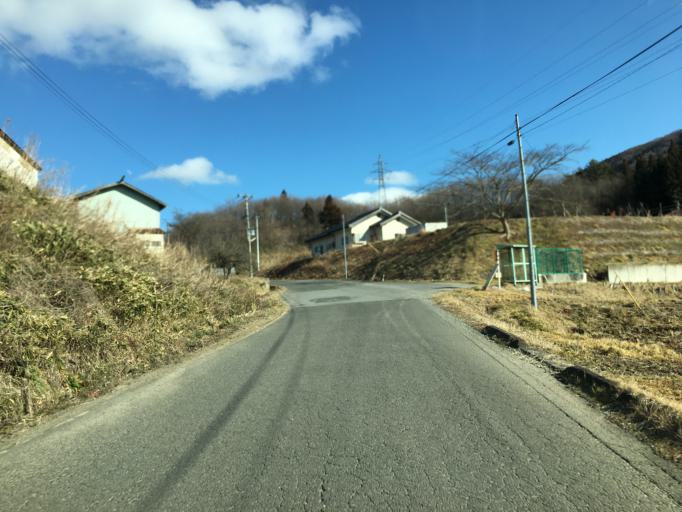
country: JP
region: Fukushima
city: Funehikimachi-funehiki
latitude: 37.4339
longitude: 140.5556
